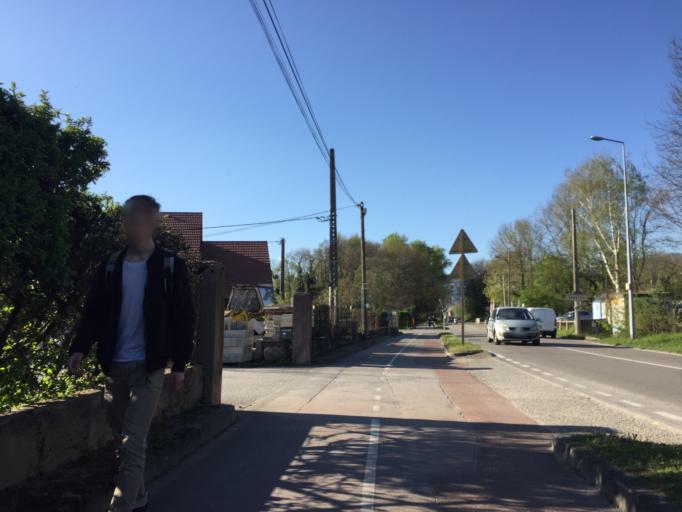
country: FR
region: Rhone-Alpes
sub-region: Departement de la Savoie
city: Barberaz
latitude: 45.5577
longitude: 5.9484
